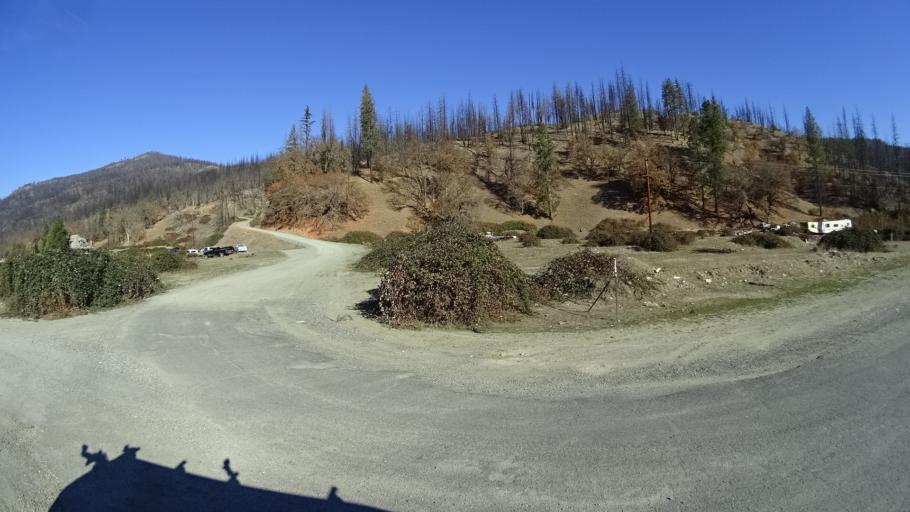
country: US
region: California
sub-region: Siskiyou County
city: Happy Camp
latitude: 41.8419
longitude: -123.0323
